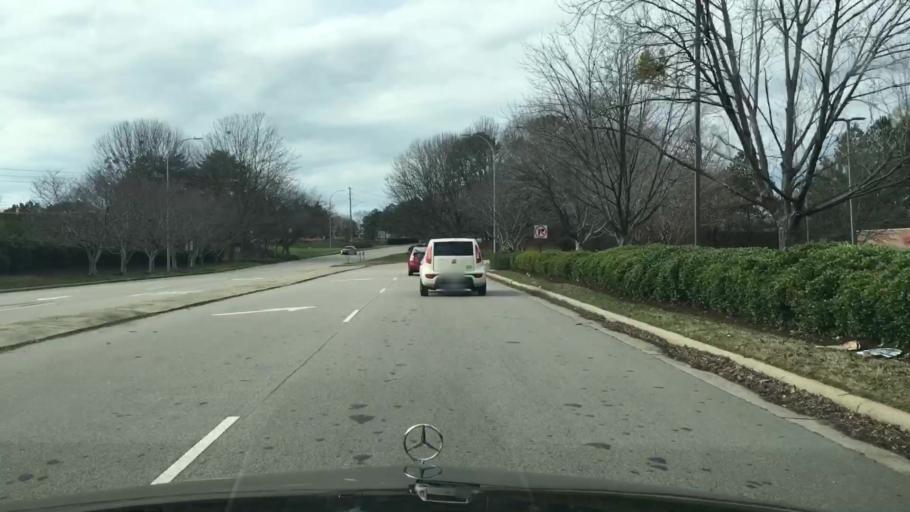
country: US
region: North Carolina
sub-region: Wake County
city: Cary
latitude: 35.7615
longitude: -78.7422
